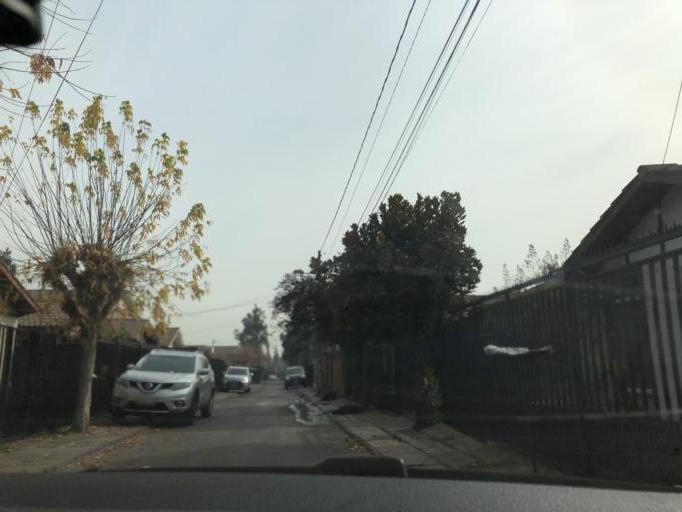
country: CL
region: Santiago Metropolitan
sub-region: Provincia de Cordillera
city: Puente Alto
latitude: -33.5502
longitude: -70.5629
